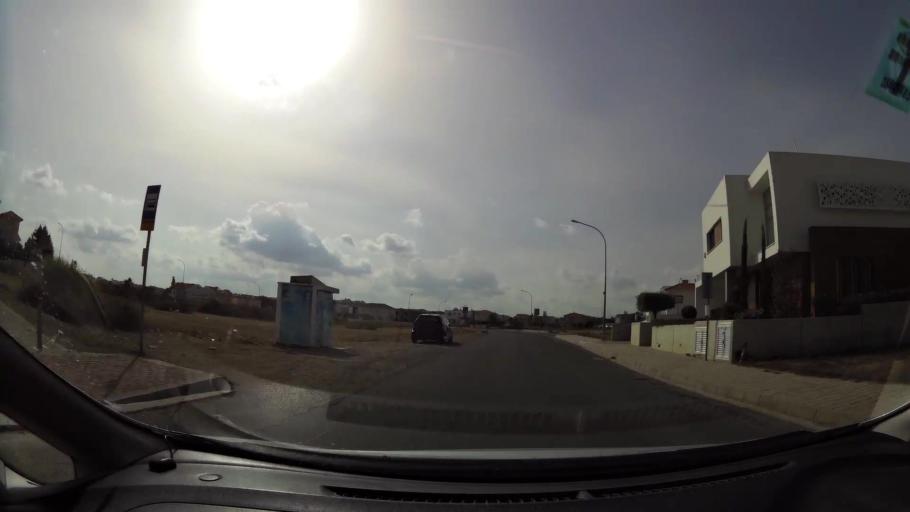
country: CY
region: Lefkosia
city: Geri
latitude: 35.0708
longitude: 33.3945
